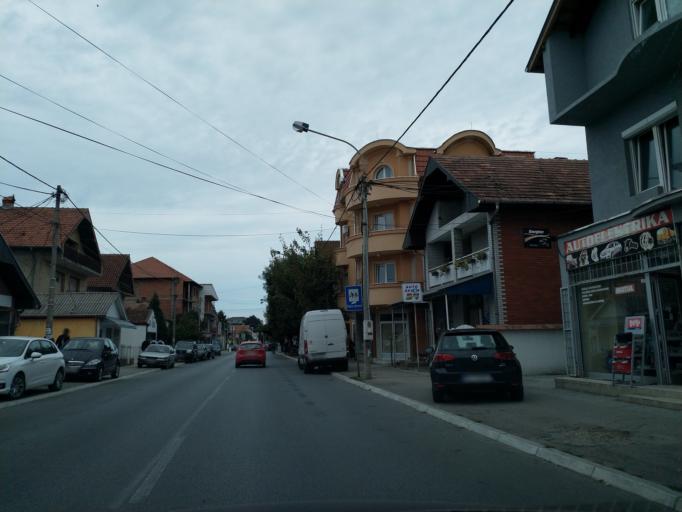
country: RS
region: Central Serbia
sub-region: Pomoravski Okrug
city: Jagodina
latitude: 43.9826
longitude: 21.2542
